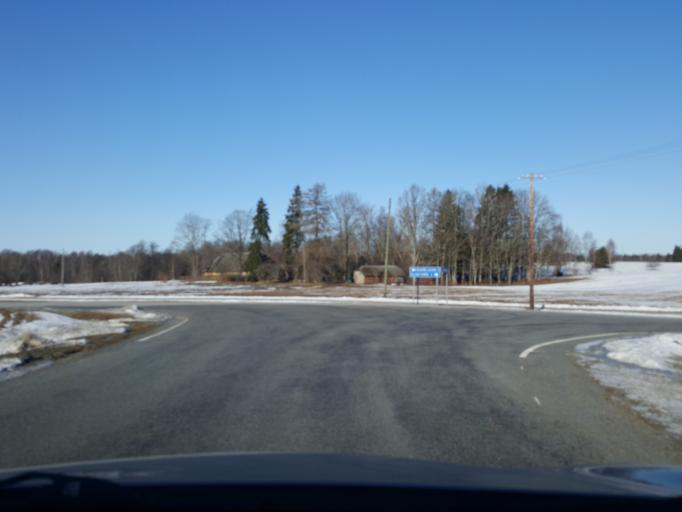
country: EE
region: Viljandimaa
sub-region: Suure-Jaani vald
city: Suure-Jaani
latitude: 58.5414
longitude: 25.5312
